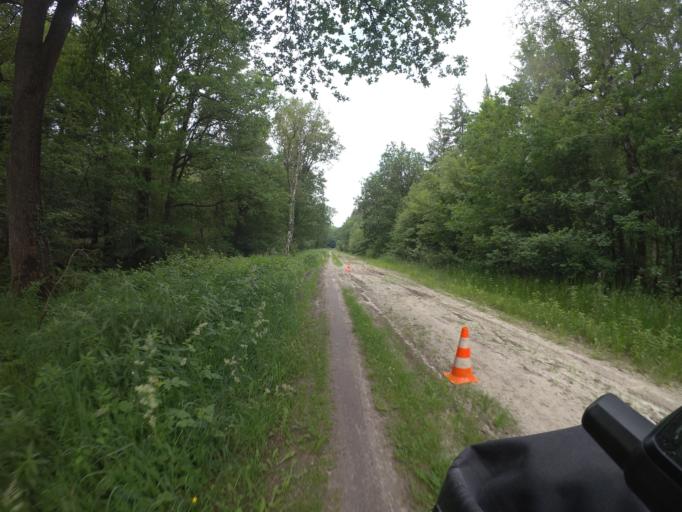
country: NL
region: Drenthe
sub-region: Gemeente Assen
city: Assen
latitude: 53.0179
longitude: 6.4183
